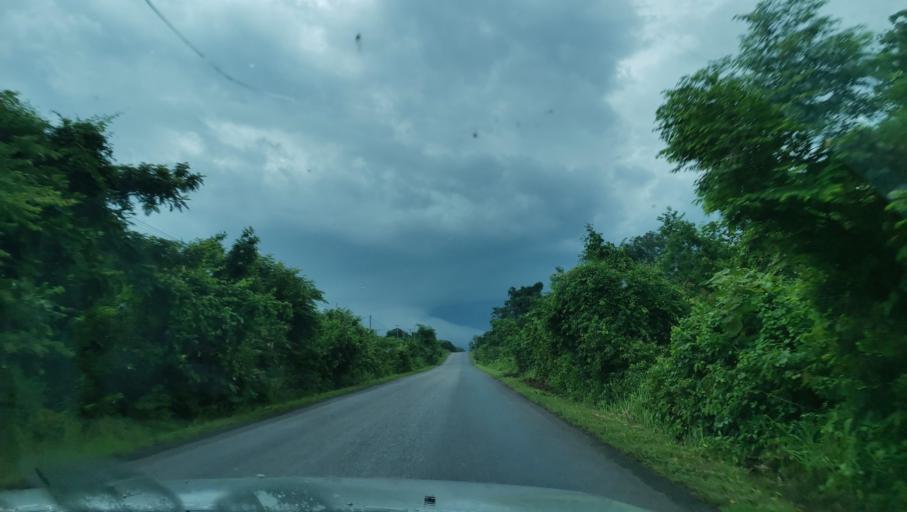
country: TH
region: Nakhon Phanom
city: Ban Phaeng
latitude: 17.8816
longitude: 104.4078
